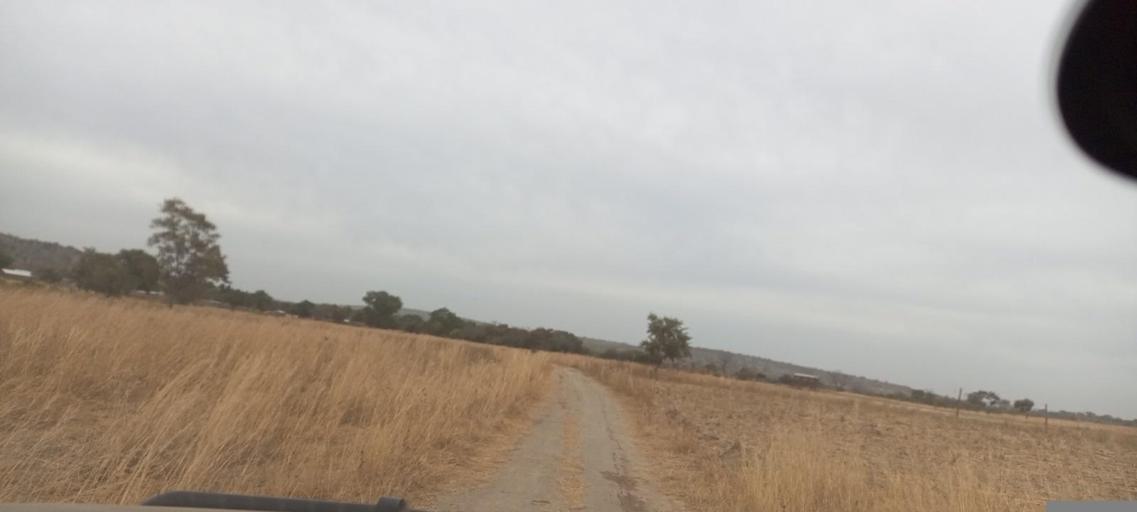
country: ML
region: Koulikoro
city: Kati
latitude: 12.7646
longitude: -8.4020
